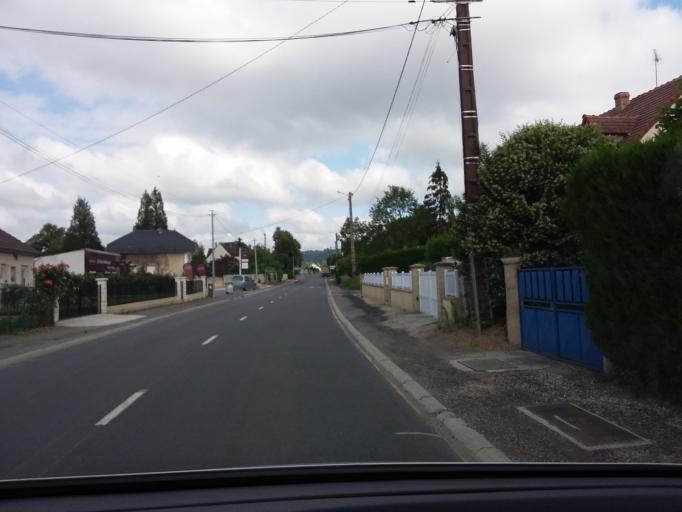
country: FR
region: Champagne-Ardenne
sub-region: Departement de la Marne
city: Fismes
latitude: 49.3887
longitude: 3.7376
